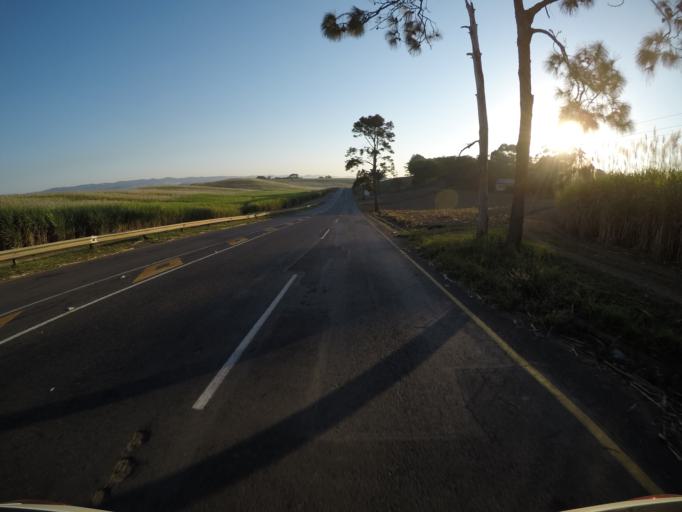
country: ZA
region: KwaZulu-Natal
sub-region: uThungulu District Municipality
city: eSikhawini
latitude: -28.9382
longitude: 31.7407
